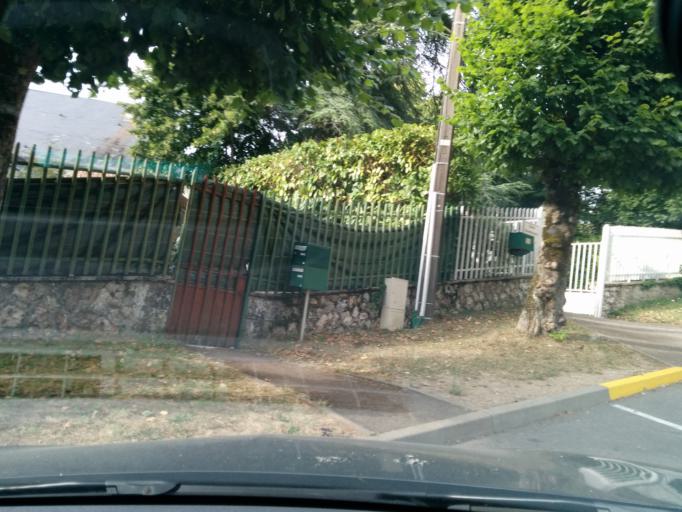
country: FR
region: Centre
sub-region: Departement du Cher
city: Sancerre
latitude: 47.3298
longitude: 2.8346
